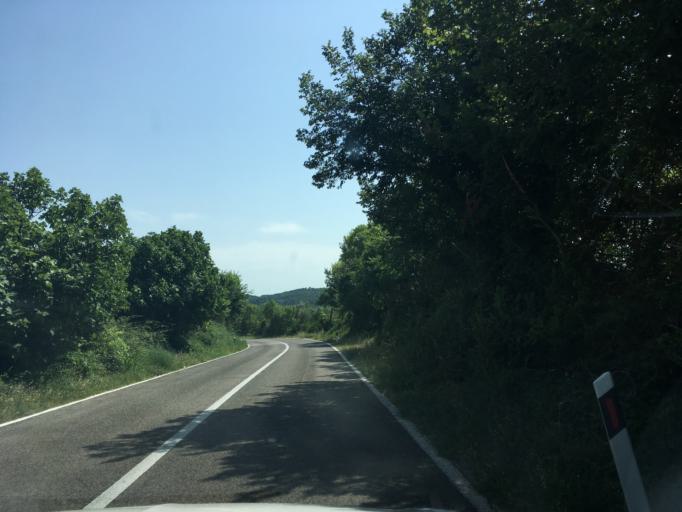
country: HR
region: Sibensko-Kniniska
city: Kistanje
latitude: 43.9336
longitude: 15.8334
